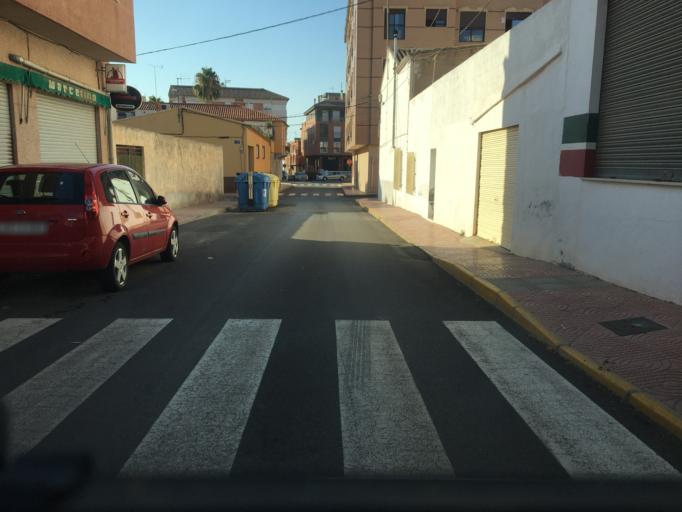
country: ES
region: Murcia
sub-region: Murcia
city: Puerto Lumbreras
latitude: 37.5662
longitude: -1.8058
